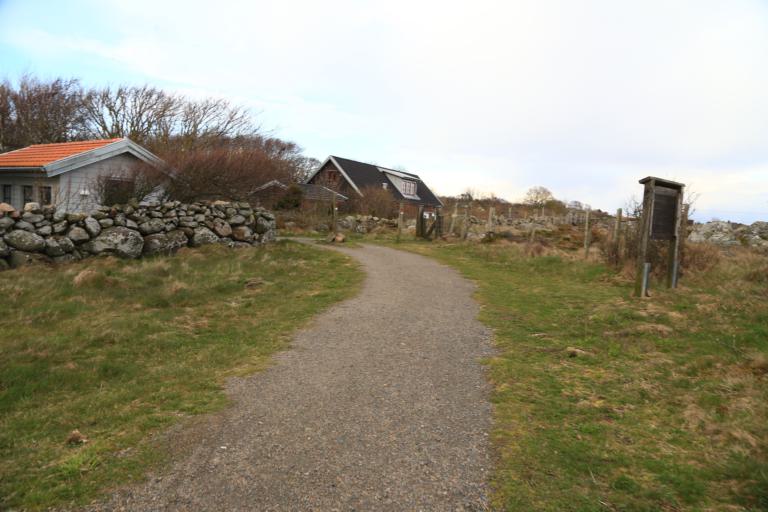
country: SE
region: Halland
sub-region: Varbergs Kommun
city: Traslovslage
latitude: 57.0511
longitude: 12.2702
